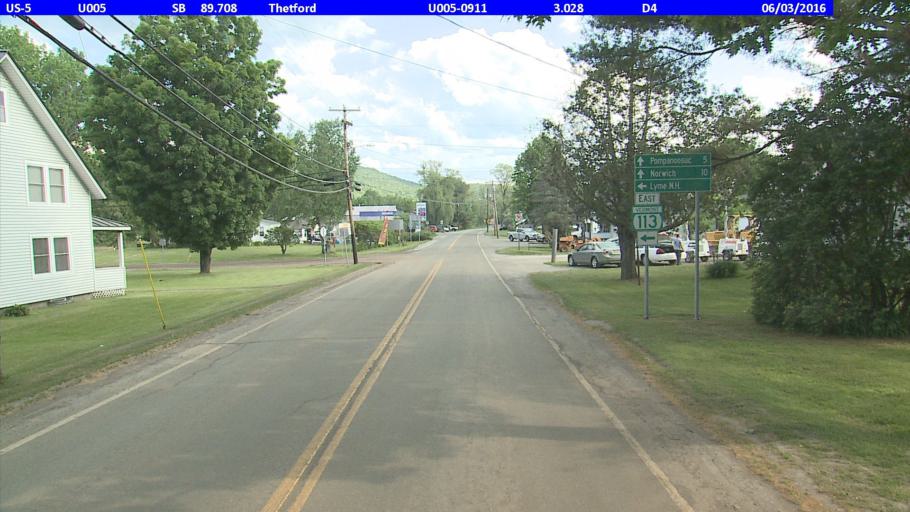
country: US
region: New Hampshire
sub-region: Grafton County
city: Lyme
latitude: 43.8121
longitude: -72.1891
